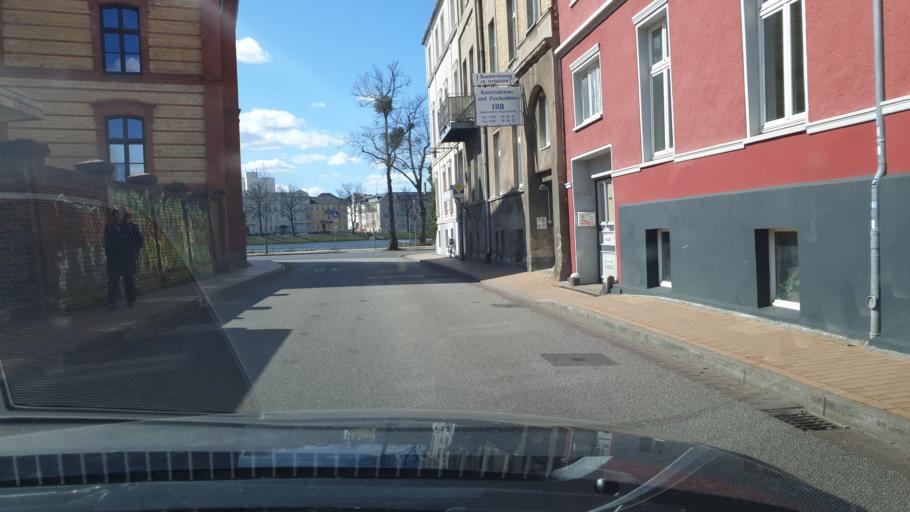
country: DE
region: Mecklenburg-Vorpommern
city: Schelfstadt
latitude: 53.6328
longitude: 11.4156
